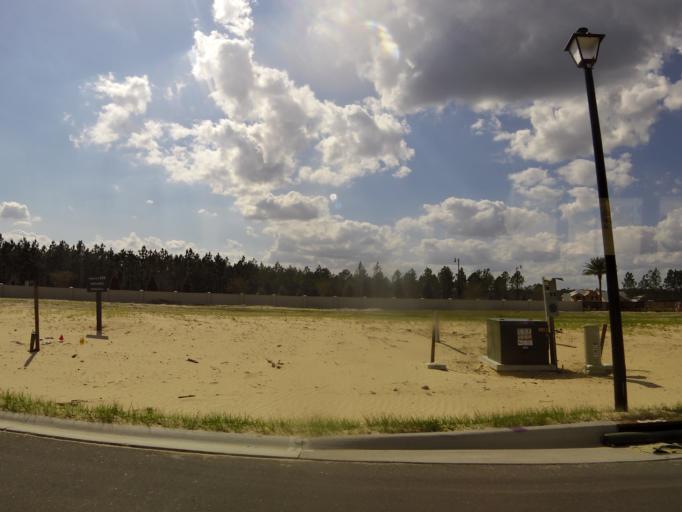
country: US
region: Florida
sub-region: Saint Johns County
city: Palm Valley
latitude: 30.1962
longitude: -81.5068
